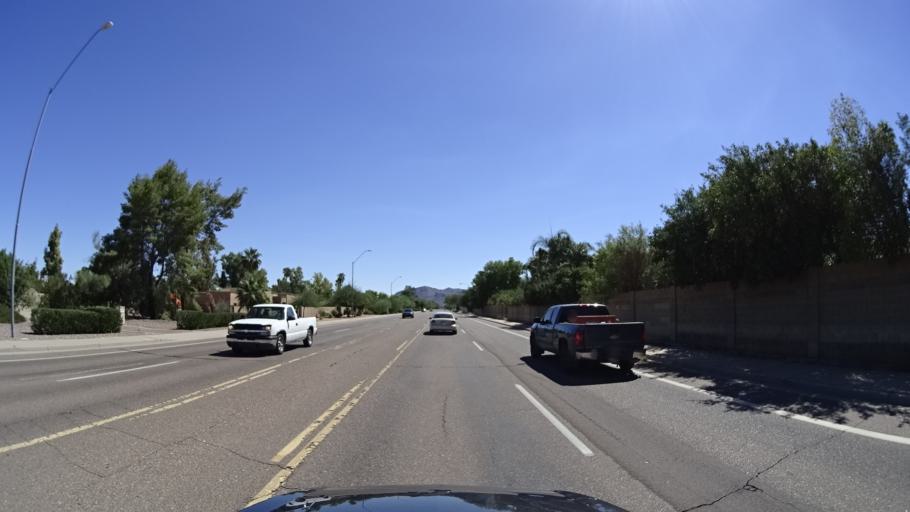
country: US
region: Arizona
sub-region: Maricopa County
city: Paradise Valley
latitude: 33.5955
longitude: -111.9606
